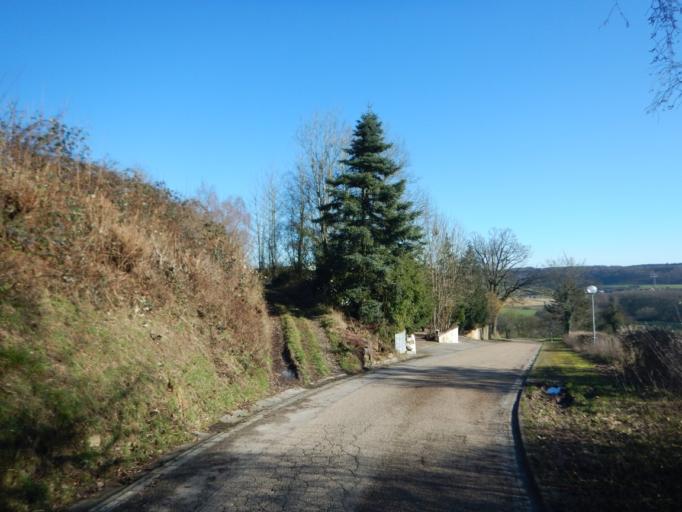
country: LU
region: Luxembourg
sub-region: Canton de Mersch
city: Lorentzweiler
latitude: 49.7027
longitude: 6.1718
